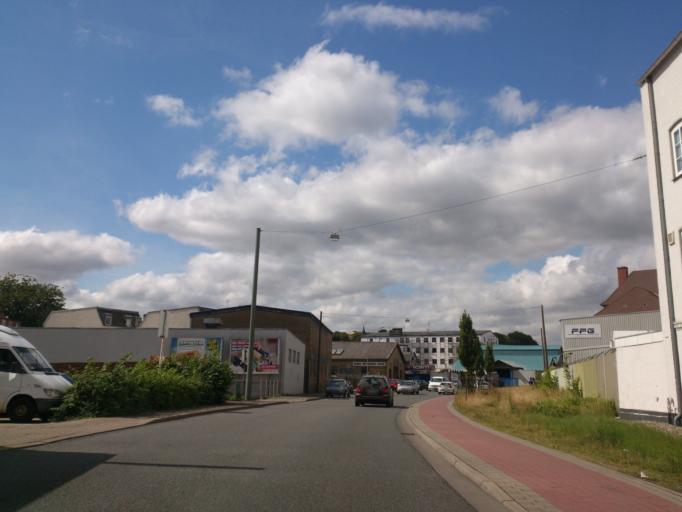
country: DE
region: Schleswig-Holstein
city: Flensburg
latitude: 54.7976
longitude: 9.4283
